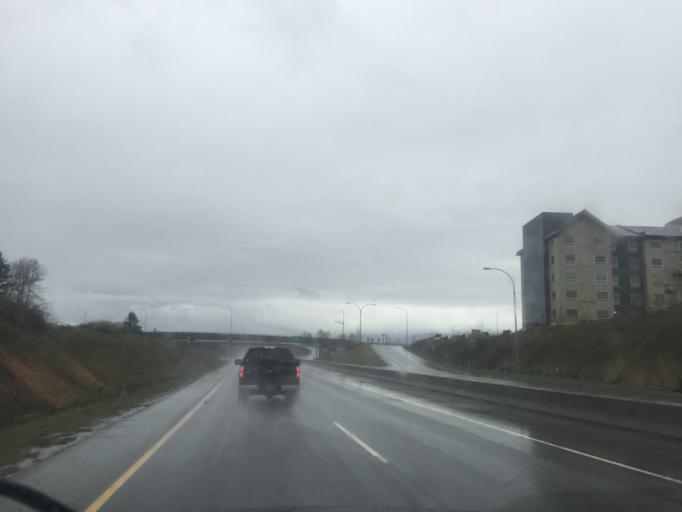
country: CA
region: British Columbia
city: Aldergrove
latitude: 49.0576
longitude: -122.3812
